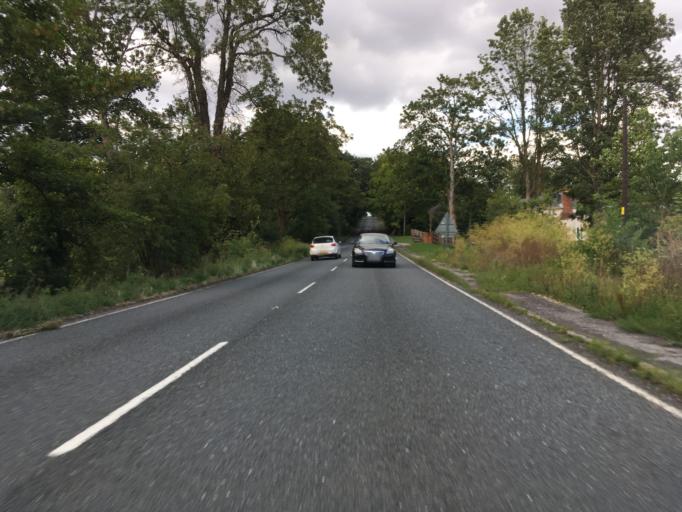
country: GB
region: England
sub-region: Hampshire
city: Kings Worthy
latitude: 51.1505
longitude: -1.2432
